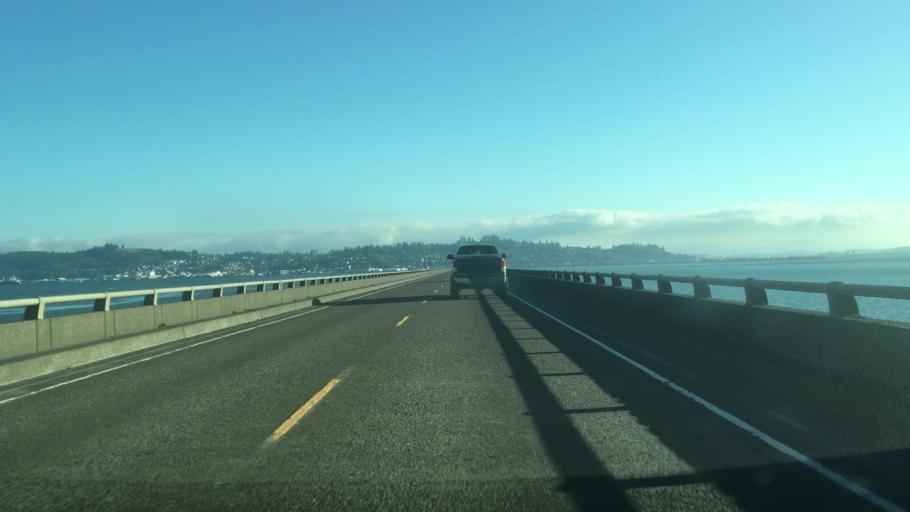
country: US
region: Oregon
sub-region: Clatsop County
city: Astoria
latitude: 46.2204
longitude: -123.8644
